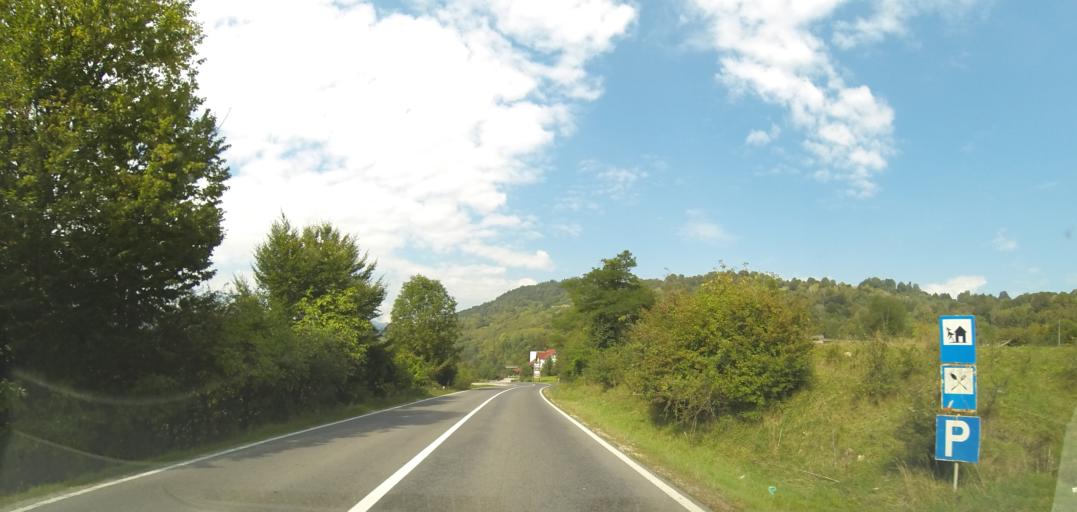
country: RO
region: Brasov
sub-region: Comuna Tarlungeni
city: Zizin
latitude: 45.5544
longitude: 25.8067
